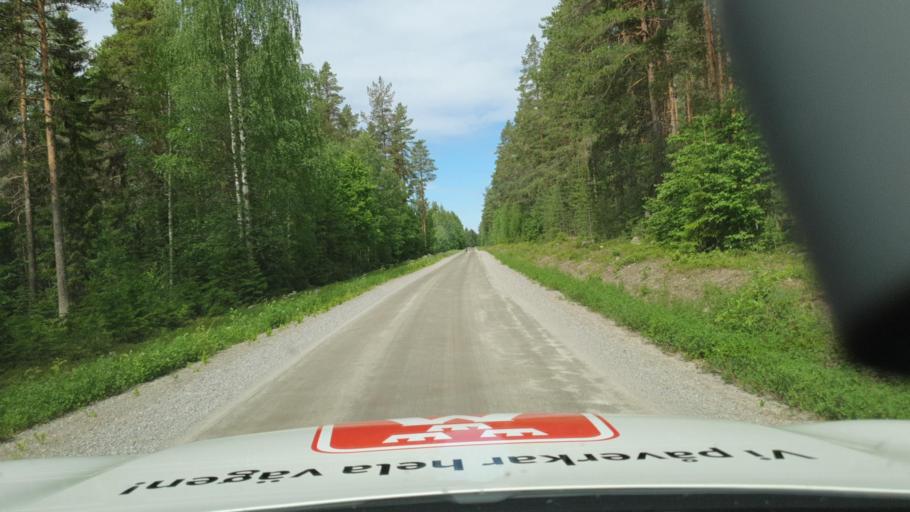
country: SE
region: Vaesterbotten
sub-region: Skelleftea Kommun
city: Burtraesk
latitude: 64.6178
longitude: 20.5731
